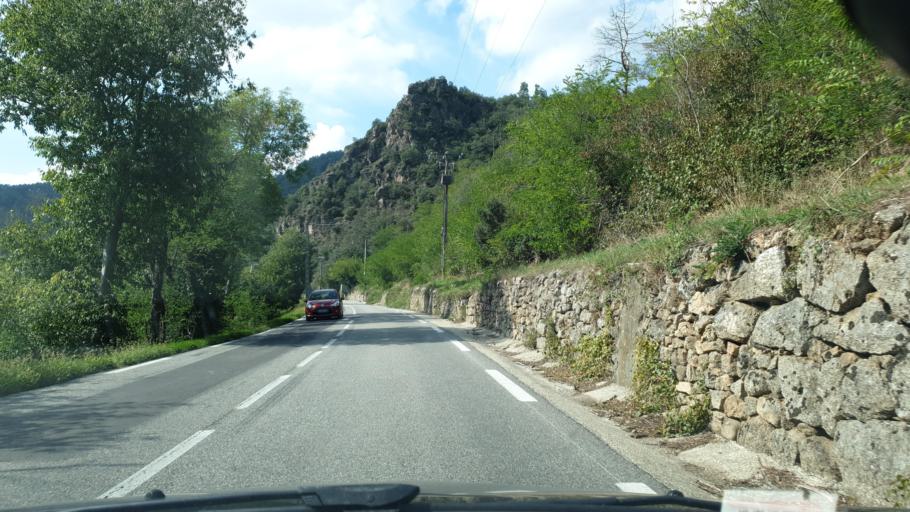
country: FR
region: Rhone-Alpes
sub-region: Departement de l'Ardeche
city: Saint-Sauveur-de-Montagut
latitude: 44.8207
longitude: 4.6435
